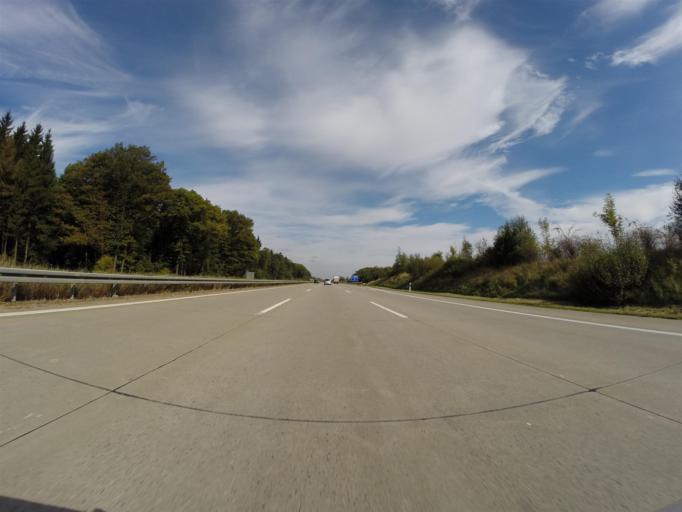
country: DE
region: Saxony
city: Rossau
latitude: 50.9620
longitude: 13.0747
